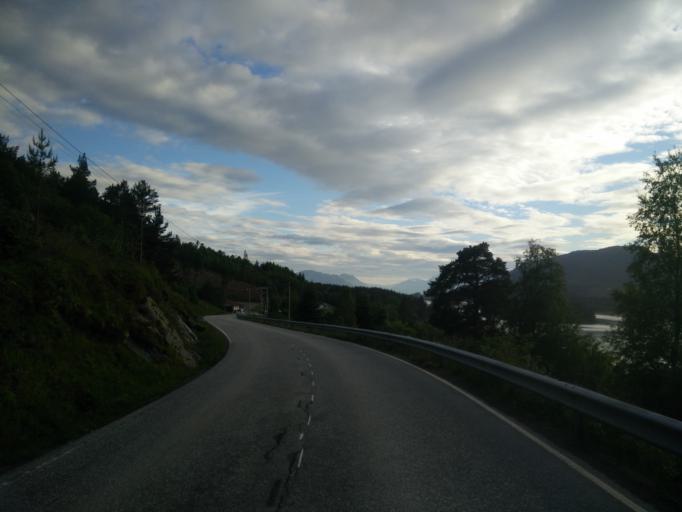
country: NO
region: More og Romsdal
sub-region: Kristiansund
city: Rensvik
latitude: 63.0192
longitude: 8.0101
